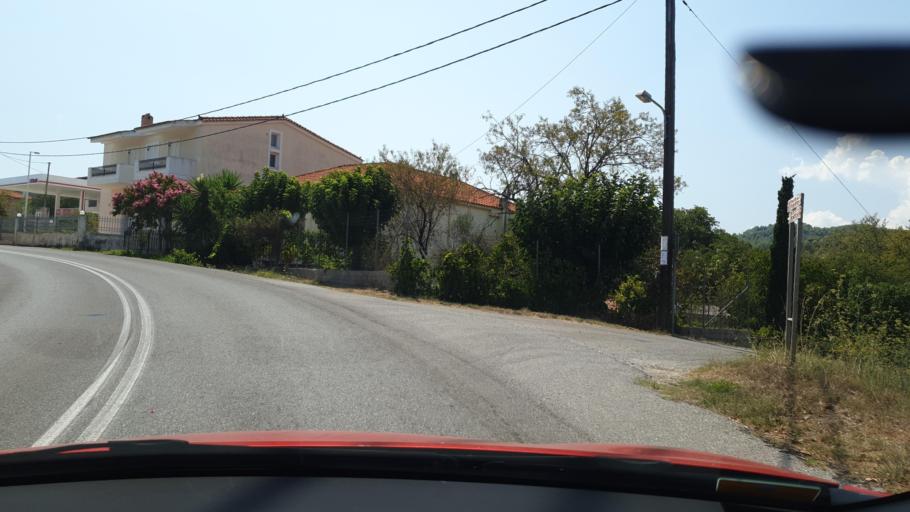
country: GR
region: Central Greece
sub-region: Nomos Evvoias
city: Oxilithos
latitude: 38.5405
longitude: 24.0756
